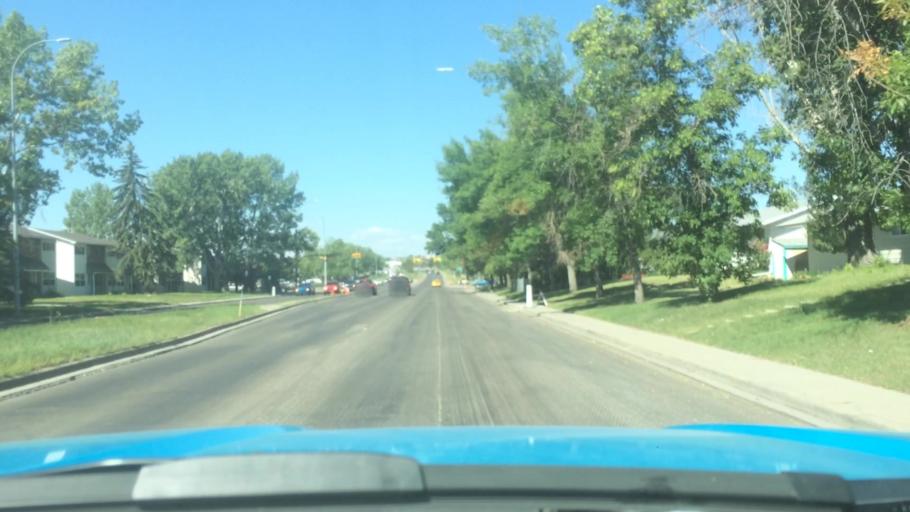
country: CA
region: Alberta
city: Calgary
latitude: 51.0530
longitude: -113.9677
